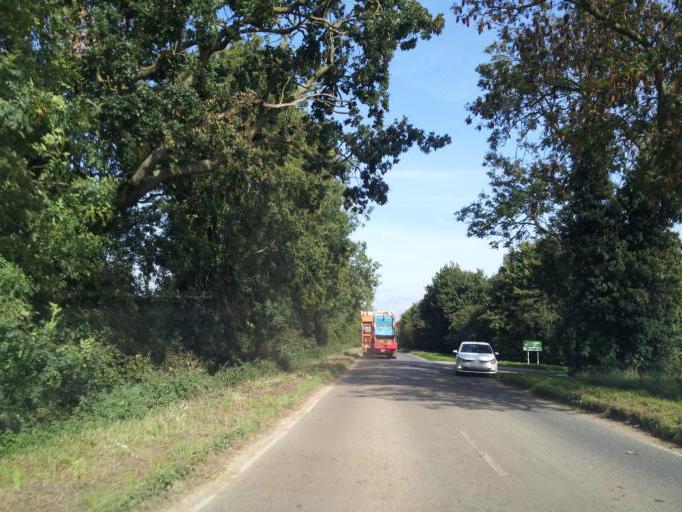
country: GB
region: England
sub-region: Cambridgeshire
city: Waterbeach
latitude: 52.2793
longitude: 0.1690
